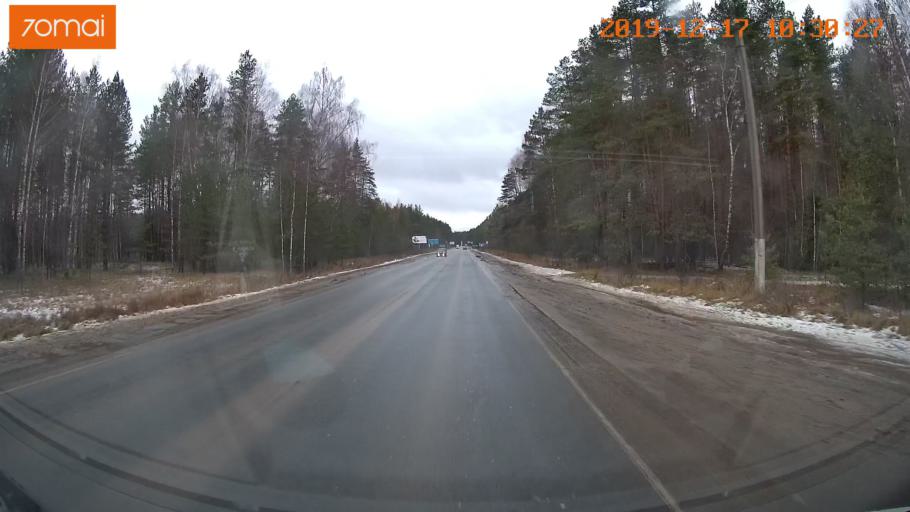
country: RU
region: Vladimir
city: Gus'-Khrustal'nyy
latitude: 55.6427
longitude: 40.7086
